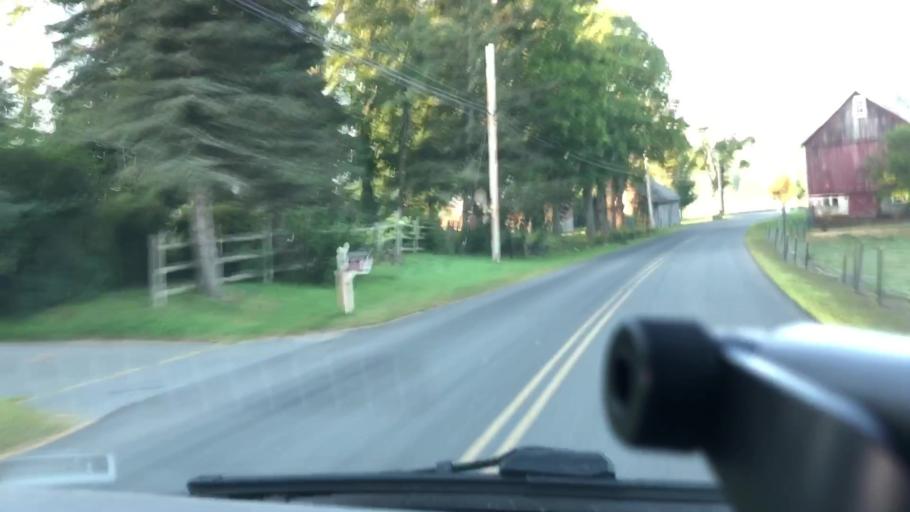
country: US
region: Massachusetts
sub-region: Franklin County
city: Ashfield
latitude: 42.5033
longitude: -72.8478
